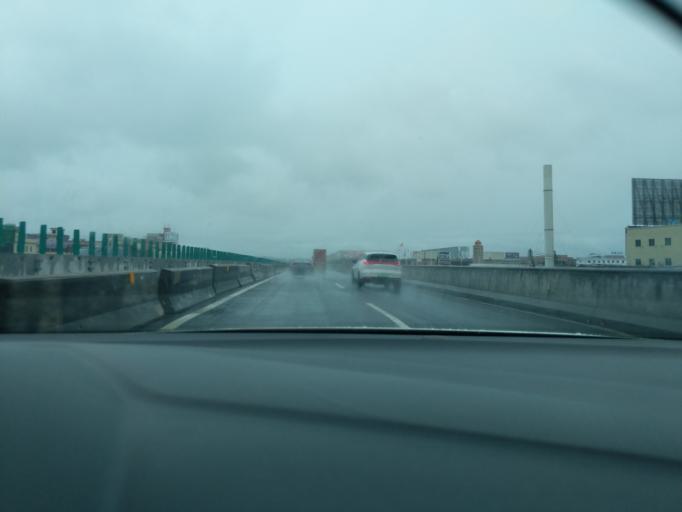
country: CN
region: Guangdong
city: Shuikou
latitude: 22.4741
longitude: 112.7644
